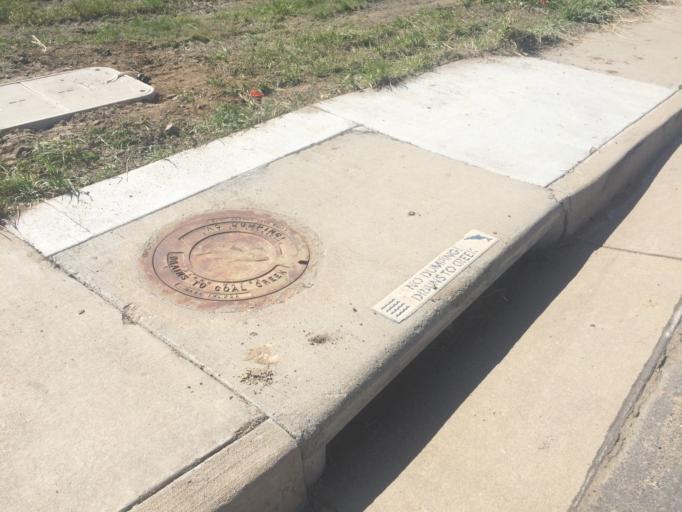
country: US
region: Colorado
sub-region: Boulder County
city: Lafayette
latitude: 40.0064
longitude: -105.1069
